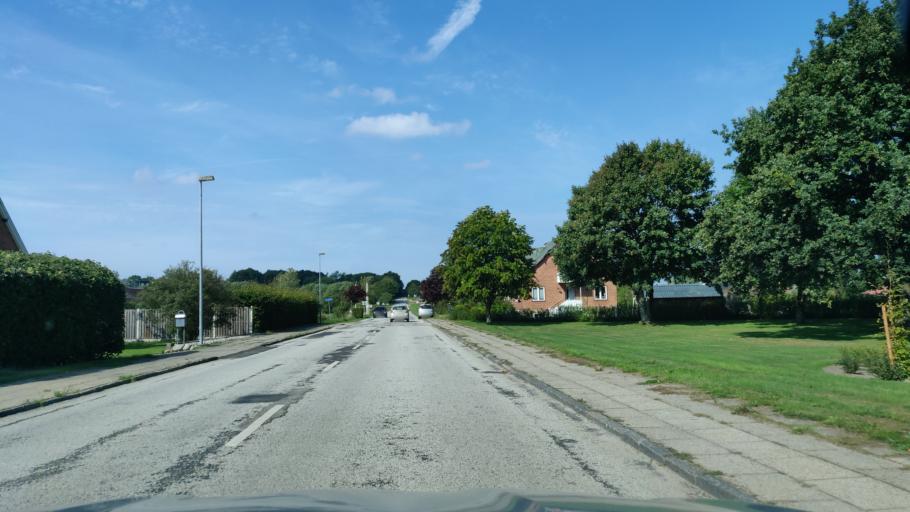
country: DK
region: Central Jutland
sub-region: Herning Kommune
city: Avlum
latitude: 56.2147
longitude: 8.8513
